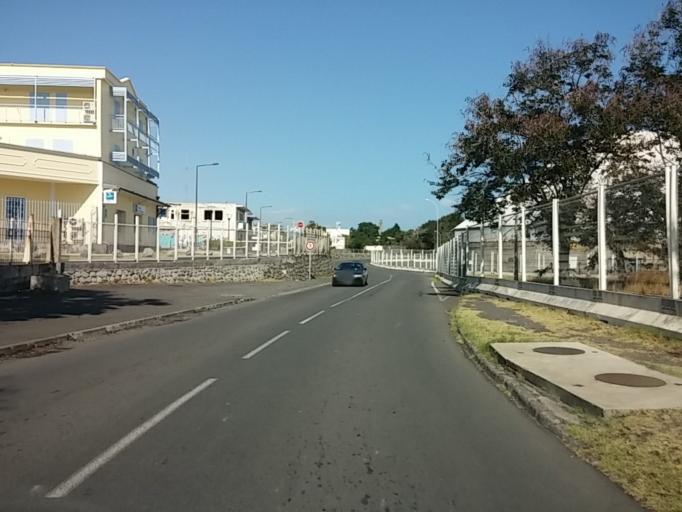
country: RE
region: Reunion
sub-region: Reunion
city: Le Port
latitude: -20.9351
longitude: 55.2897
